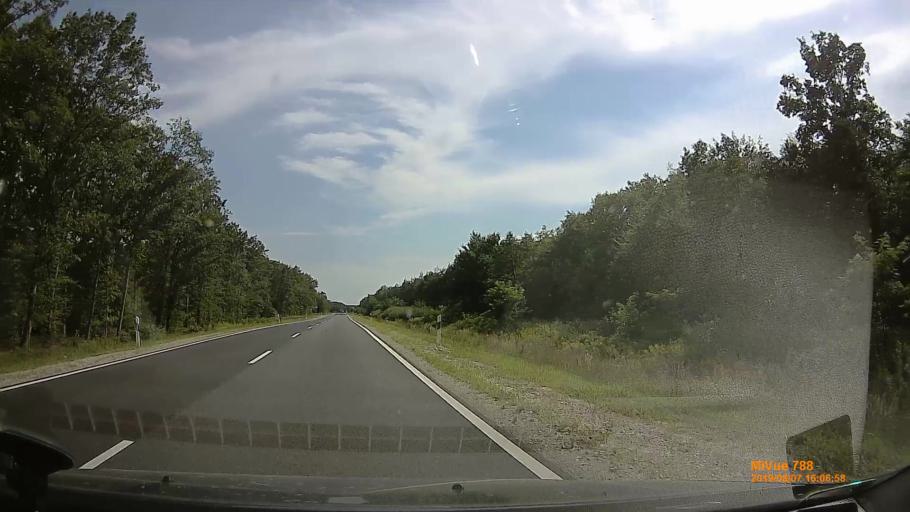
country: HU
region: Zala
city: Zalalovo
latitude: 46.9286
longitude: 16.6003
